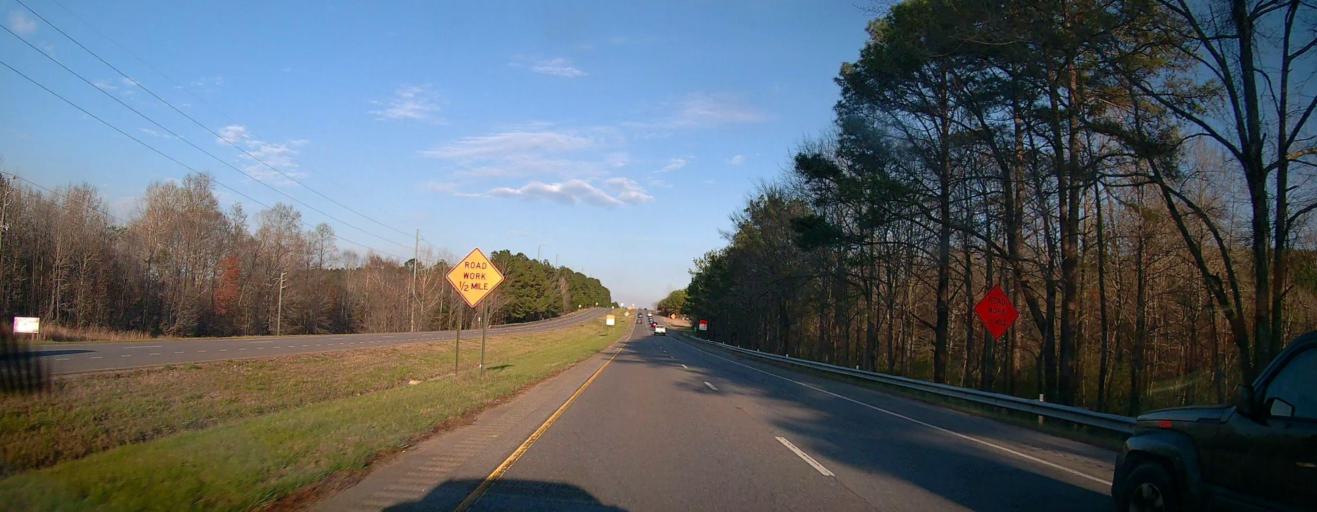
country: US
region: Alabama
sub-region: Shelby County
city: Chelsea
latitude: 33.3504
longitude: -86.5934
